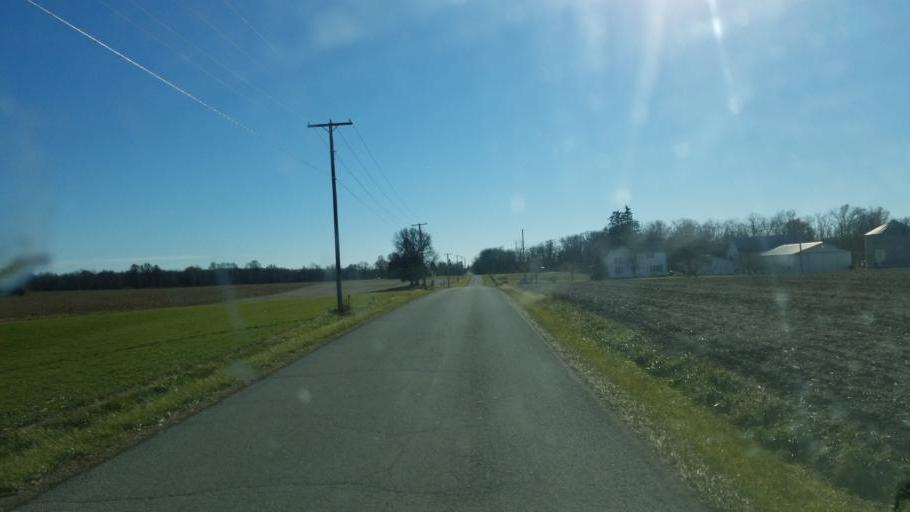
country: US
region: Ohio
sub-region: Crawford County
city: Galion
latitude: 40.7325
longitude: -82.8490
